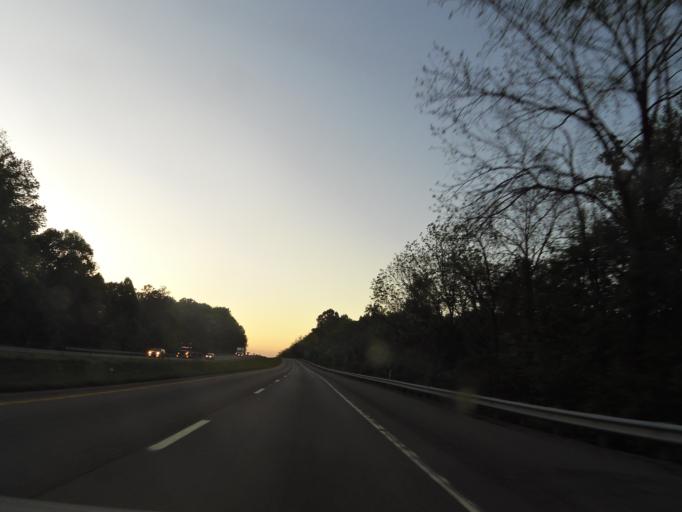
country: US
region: Tennessee
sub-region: Cocke County
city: Newport
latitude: 35.9309
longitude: -83.1925
